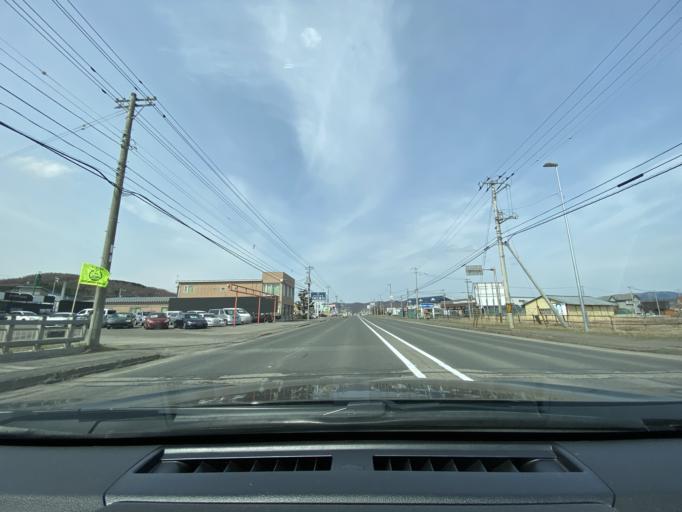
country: JP
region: Hokkaido
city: Kitami
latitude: 43.8002
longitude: 143.8257
